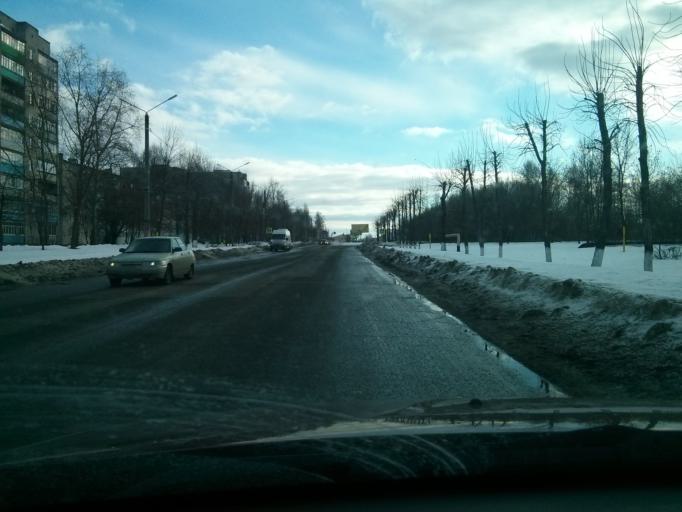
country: RU
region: Vladimir
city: Murom
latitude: 55.5516
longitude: 42.0628
